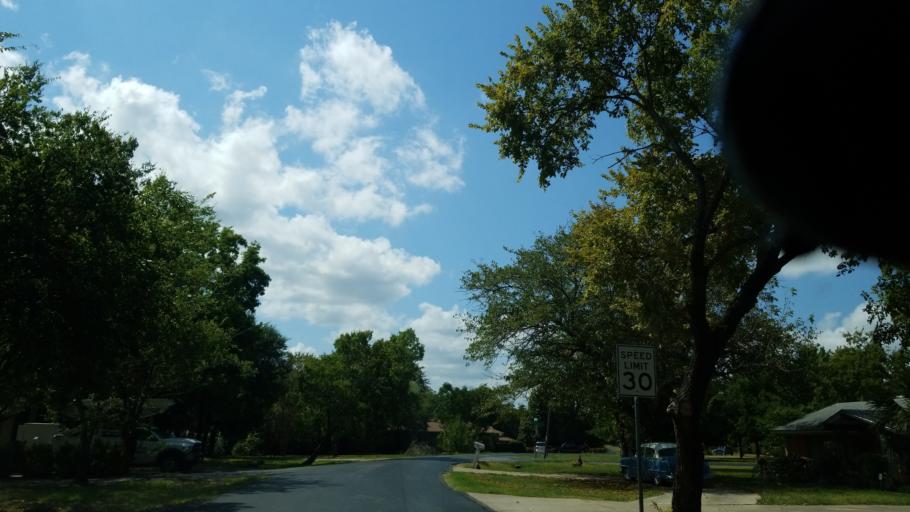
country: US
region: Texas
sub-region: Dallas County
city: Grand Prairie
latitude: 32.7150
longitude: -96.9955
